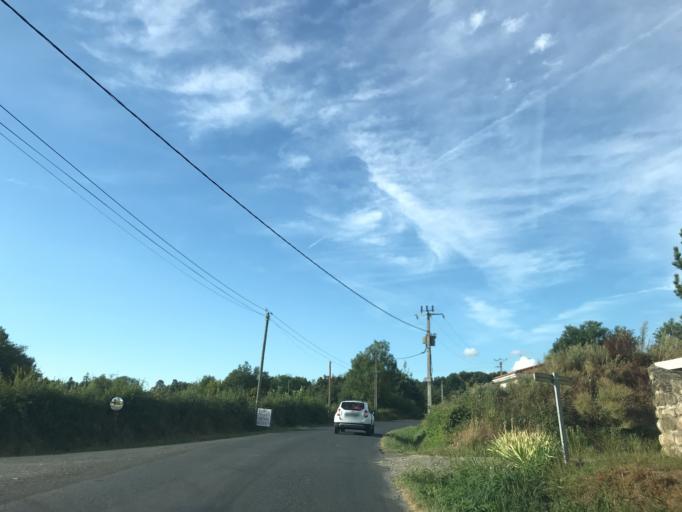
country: FR
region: Auvergne
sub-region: Departement du Puy-de-Dome
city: Peschadoires
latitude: 45.8226
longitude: 3.5263
